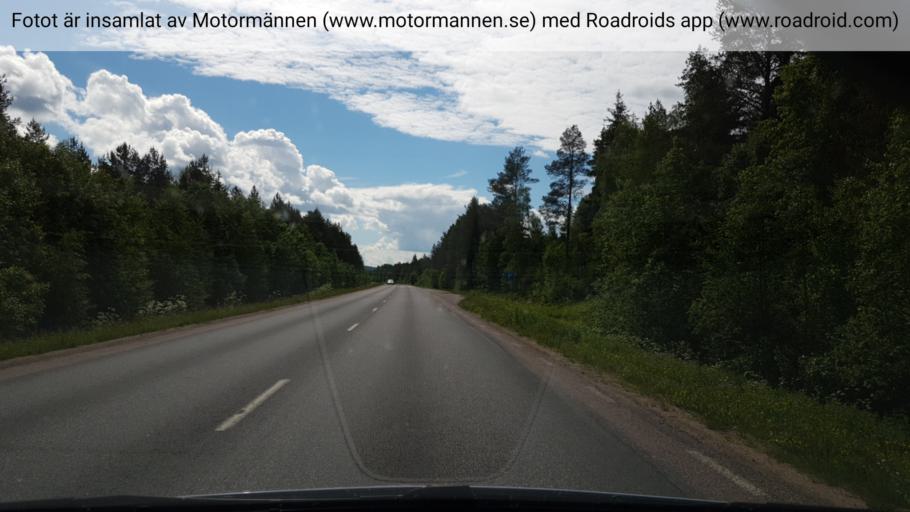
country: SE
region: Norrbotten
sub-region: Overtornea Kommun
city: OEvertornea
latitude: 66.4409
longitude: 23.6180
